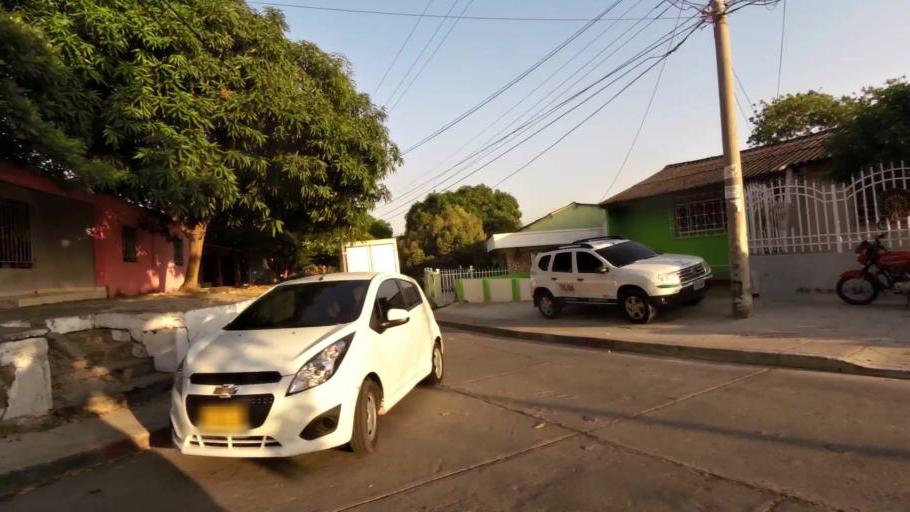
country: CO
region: Bolivar
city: Cartagena
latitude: 10.3878
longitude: -75.4840
